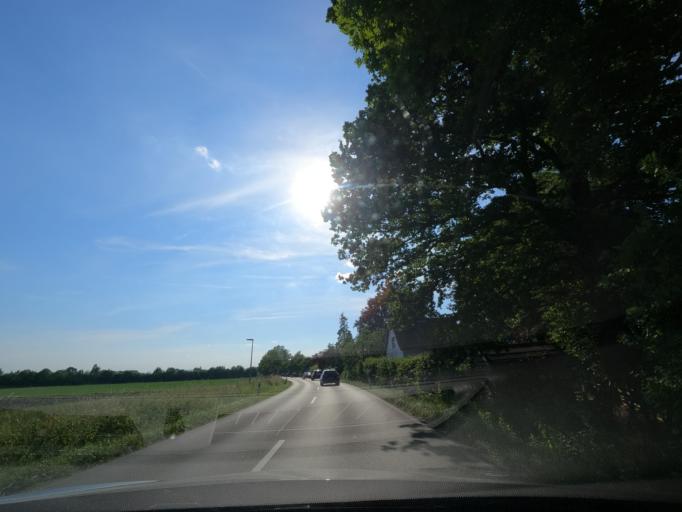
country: DE
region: Schleswig-Holstein
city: Prisdorf
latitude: 53.6599
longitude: 9.7627
